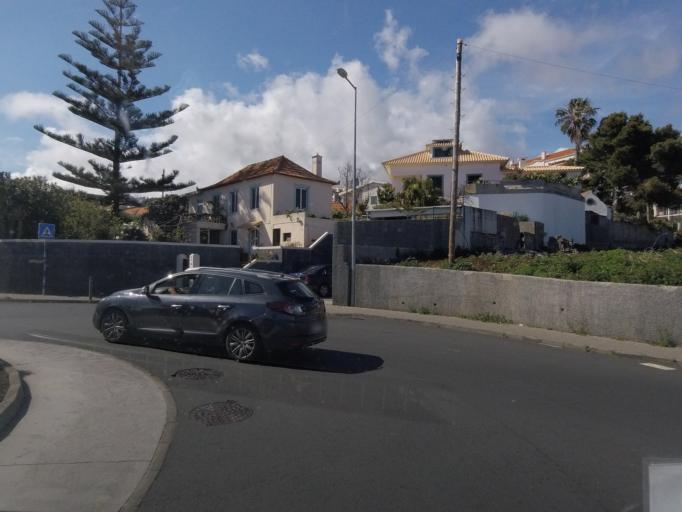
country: PT
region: Madeira
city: Canico
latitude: 32.6424
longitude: -16.8495
